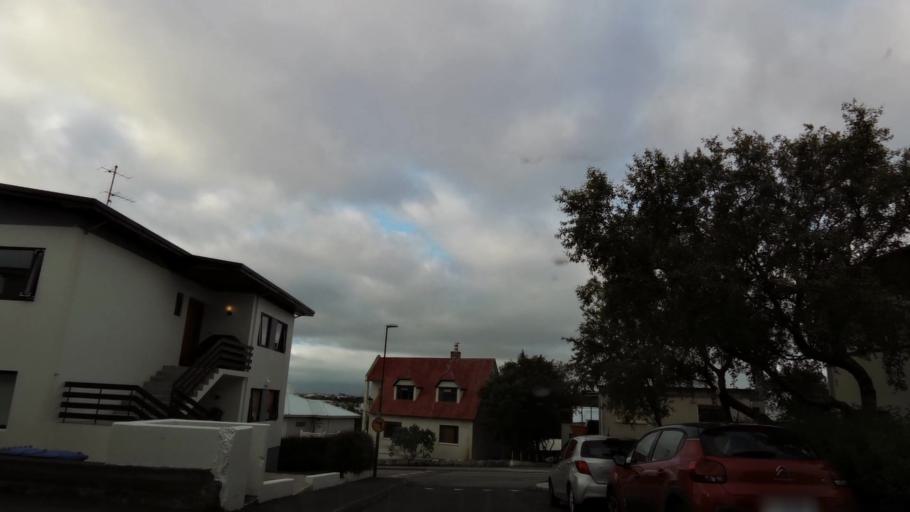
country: IS
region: Capital Region
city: Hafnarfjoerdur
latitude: 64.0646
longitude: -21.9463
